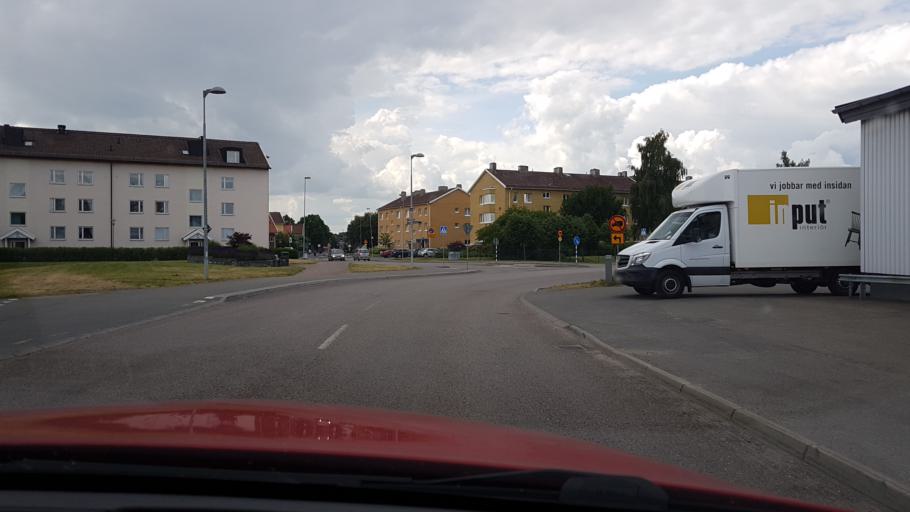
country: SE
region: Vaestra Goetaland
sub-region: Skovde Kommun
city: Skoevde
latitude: 58.4013
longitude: 13.8490
